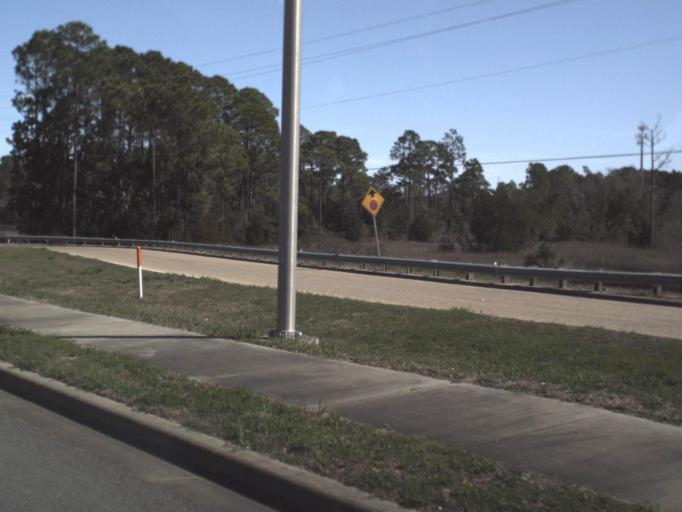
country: US
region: Florida
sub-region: Bay County
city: Lynn Haven
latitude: 30.2654
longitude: -85.6456
